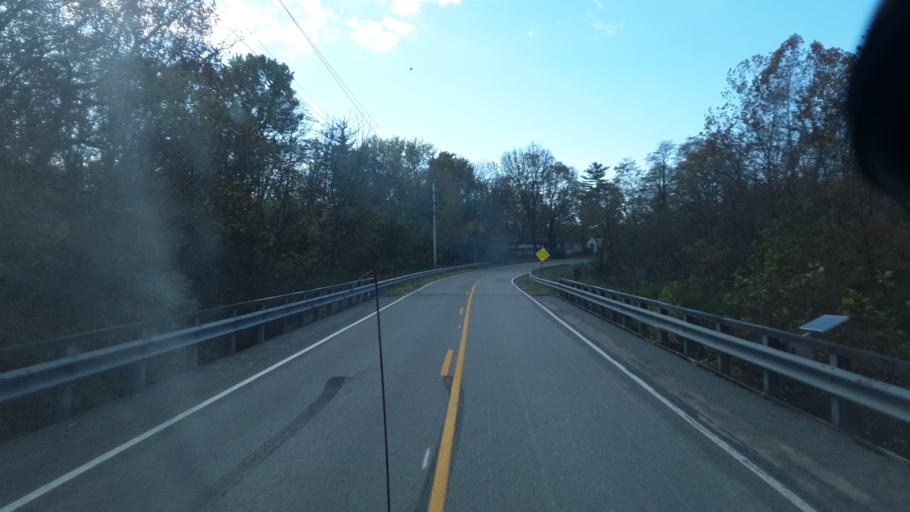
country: US
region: Ohio
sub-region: Highland County
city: Leesburg
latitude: 39.3290
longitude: -83.4742
